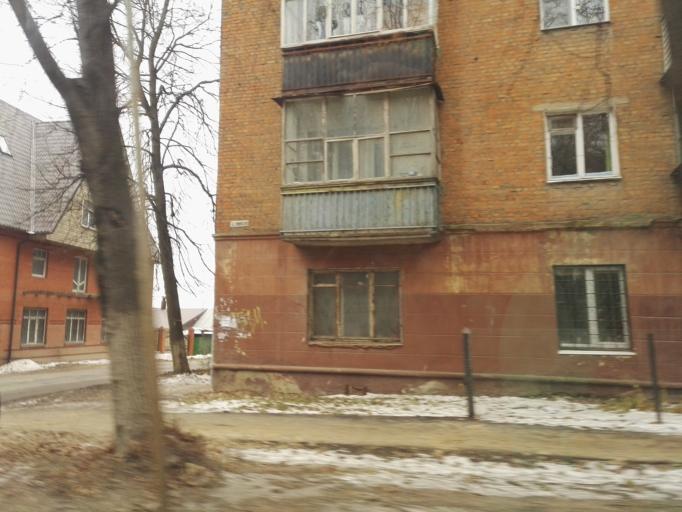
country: RU
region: Tula
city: Tula
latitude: 54.1774
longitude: 37.6145
